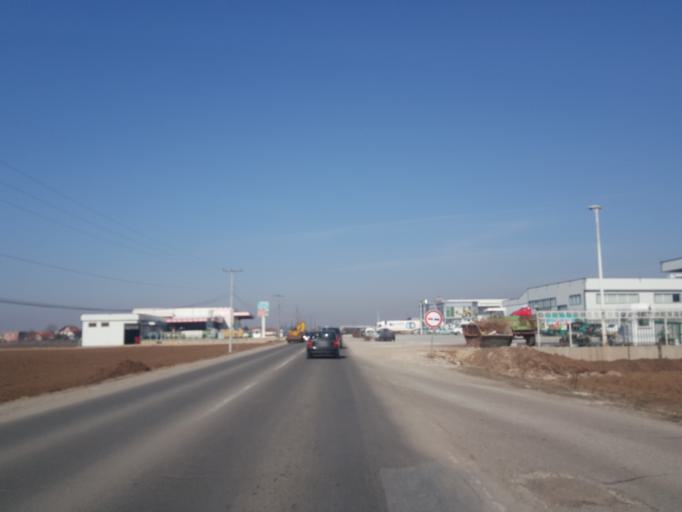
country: XK
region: Mitrovica
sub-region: Vushtrri
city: Vushtrri
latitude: 42.7830
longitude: 21.0112
